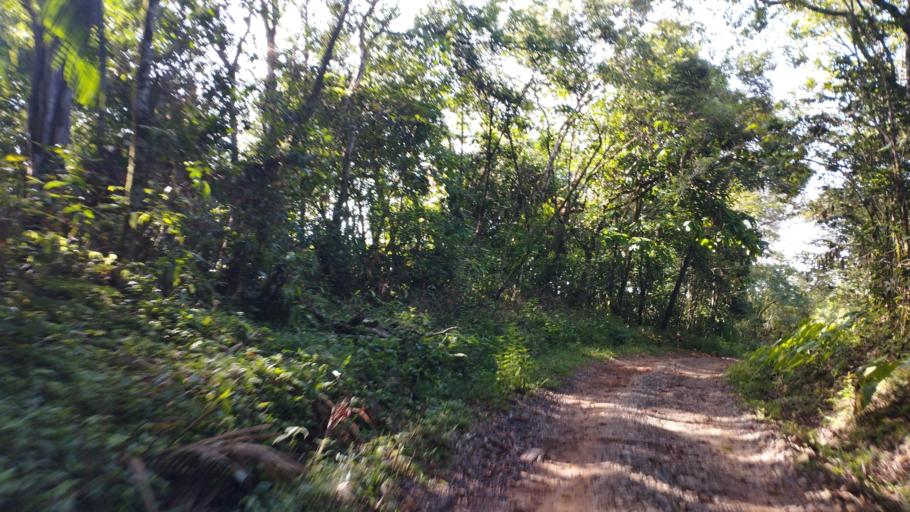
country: CO
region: Casanare
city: Sabanalarga
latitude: 4.7699
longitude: -73.0809
